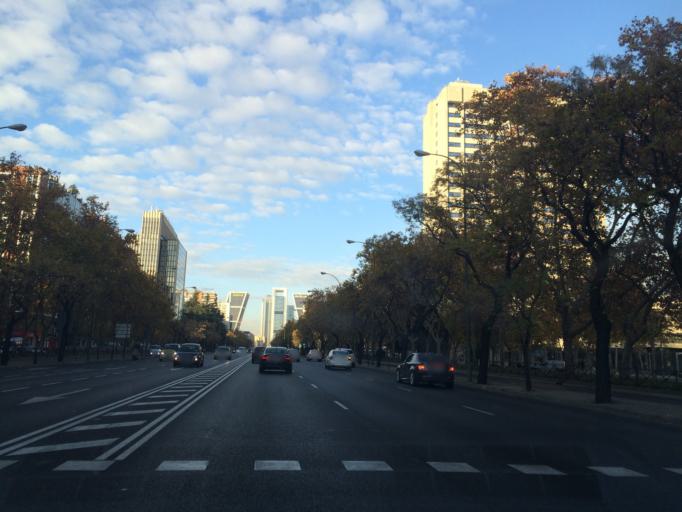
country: ES
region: Madrid
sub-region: Provincia de Madrid
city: Chamartin
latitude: 40.4565
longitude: -3.6902
